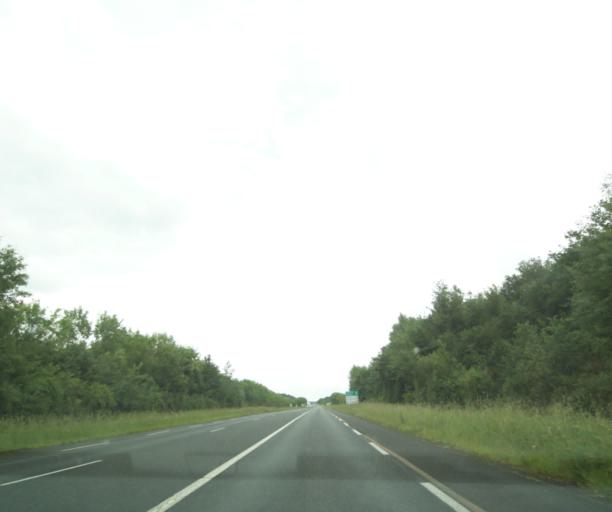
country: FR
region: Poitou-Charentes
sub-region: Departement des Deux-Sevres
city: Airvault
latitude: 46.7950
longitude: -0.2136
